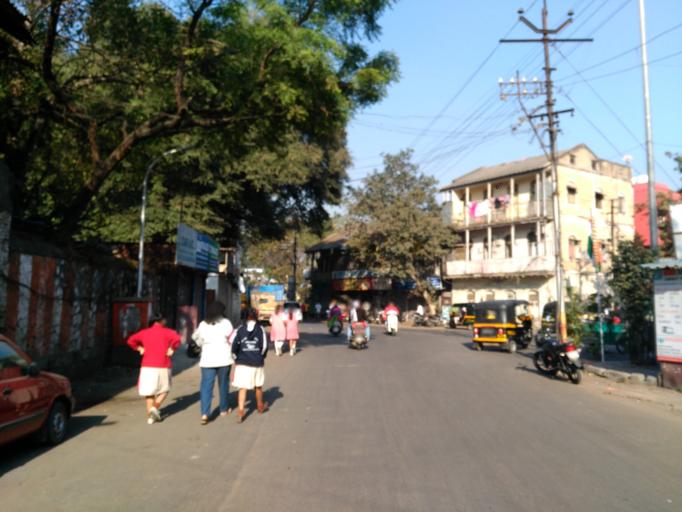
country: IN
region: Maharashtra
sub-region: Pune Division
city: Pune
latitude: 18.5163
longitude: 73.8742
